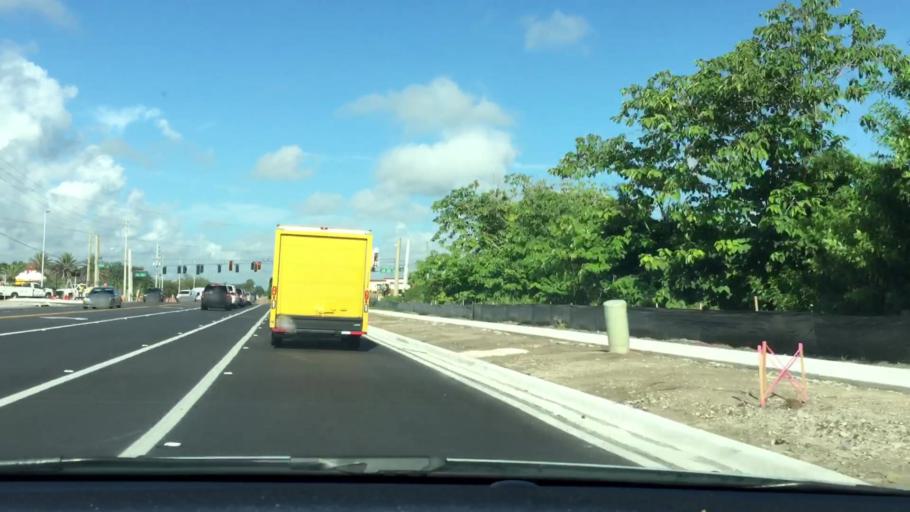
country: US
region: Florida
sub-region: Osceola County
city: Buenaventura Lakes
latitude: 28.2789
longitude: -81.3418
